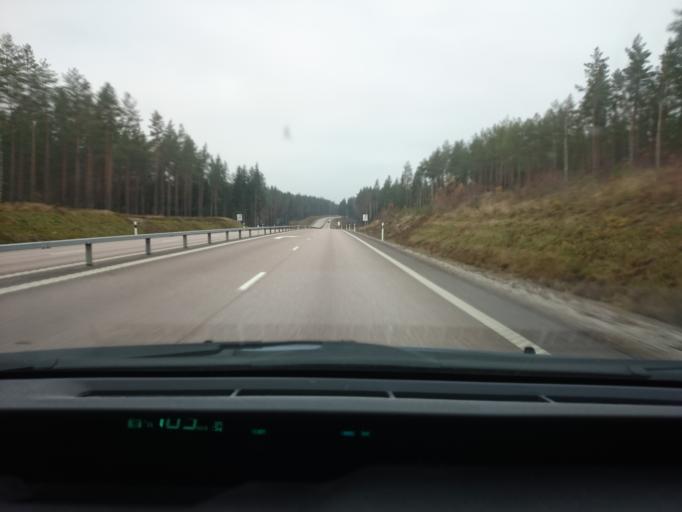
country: SE
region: Vaestmanland
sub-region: Sala Kommun
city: Sala
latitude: 60.0112
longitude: 16.3874
